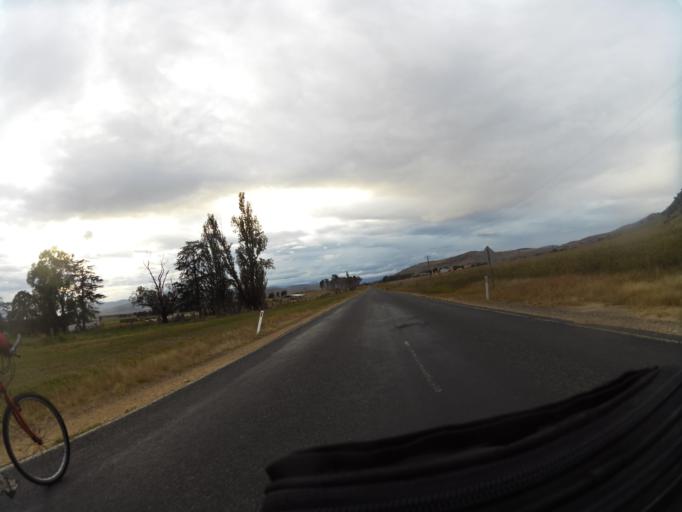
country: AU
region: New South Wales
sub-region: Greater Hume Shire
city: Holbrook
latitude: -36.0554
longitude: 147.9392
